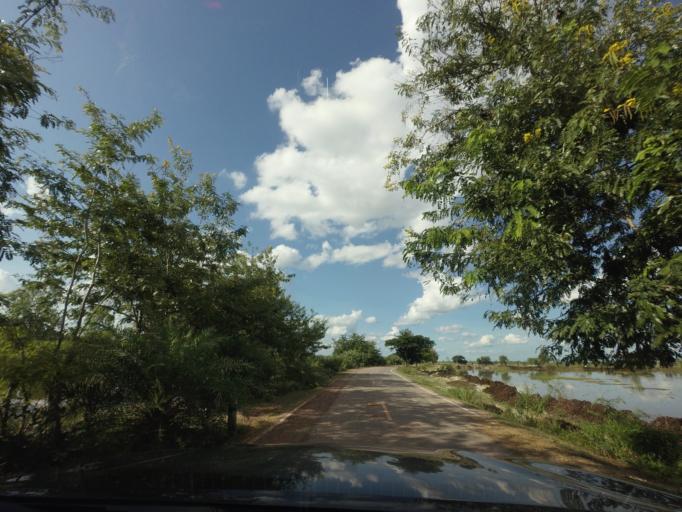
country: TH
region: Changwat Udon Thani
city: Ban Dung
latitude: 17.7483
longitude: 103.3574
